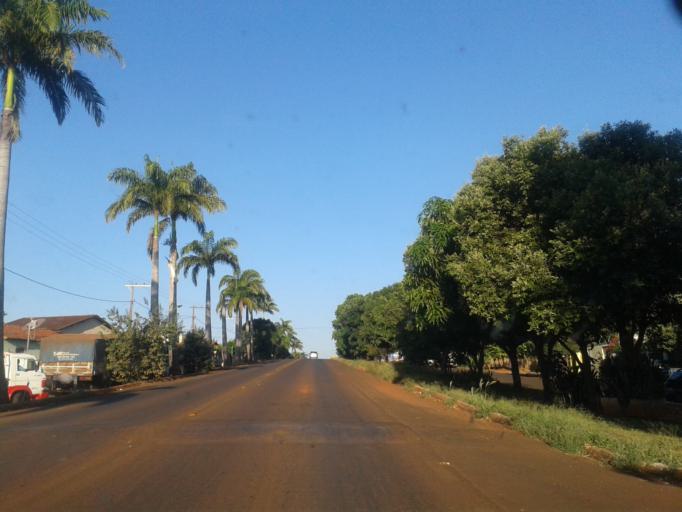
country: BR
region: Minas Gerais
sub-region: Capinopolis
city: Capinopolis
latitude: -18.6885
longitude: -49.5667
